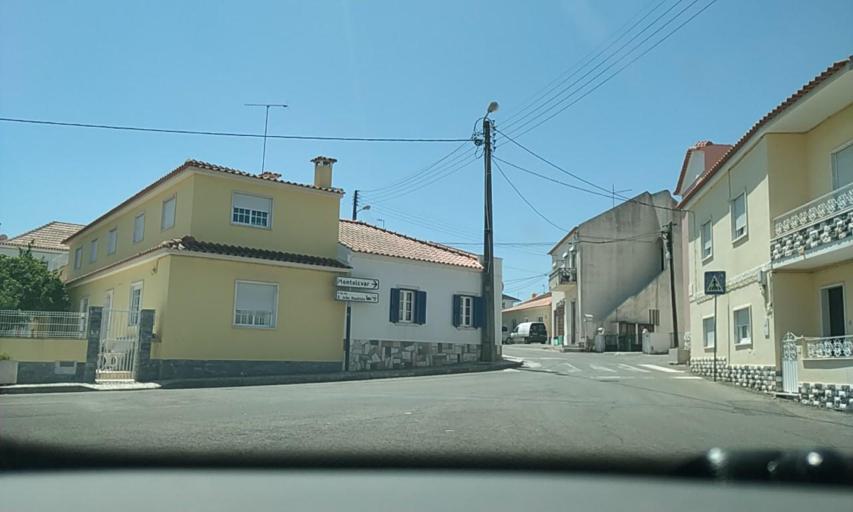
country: PT
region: Lisbon
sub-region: Sintra
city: Pero Pinheiro
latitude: 38.8662
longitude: -9.3143
